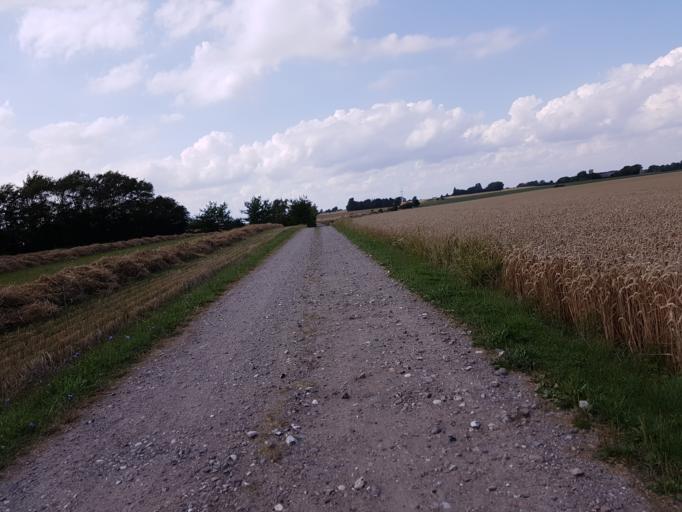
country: DK
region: Zealand
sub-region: Guldborgsund Kommune
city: Nykobing Falster
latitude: 54.5972
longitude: 11.9283
